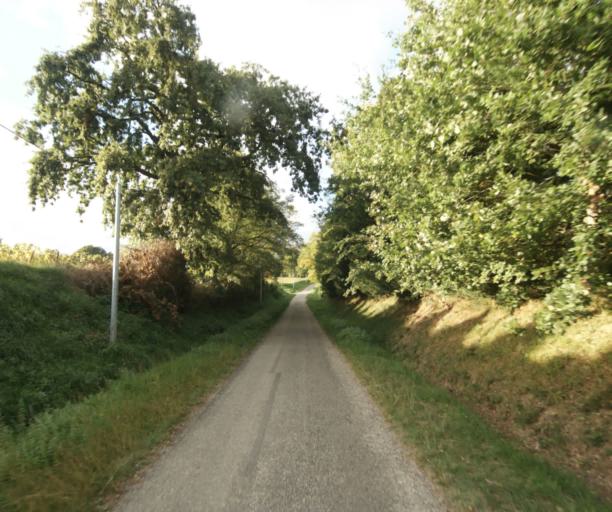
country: FR
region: Aquitaine
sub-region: Departement des Landes
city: Gabarret
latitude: 43.9489
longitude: 0.0763
